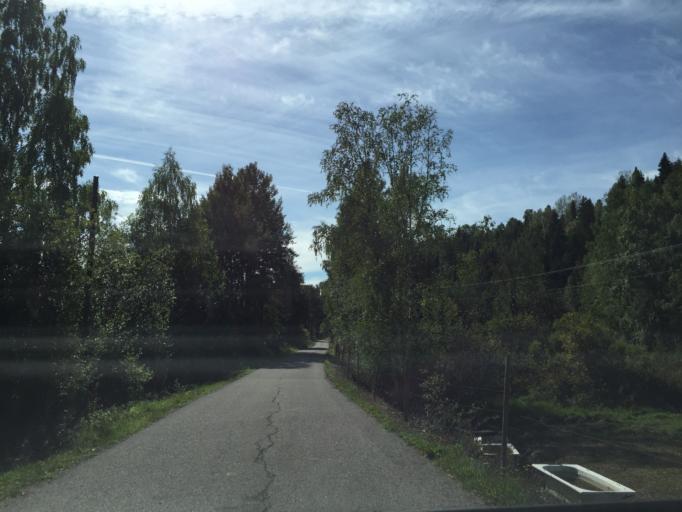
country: NO
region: Vestfold
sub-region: Hof
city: Hof
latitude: 59.4710
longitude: 10.1441
